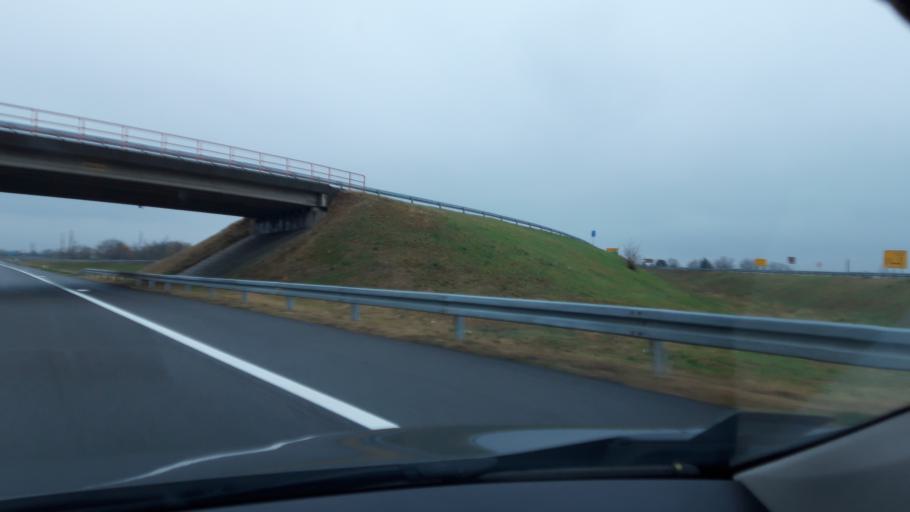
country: HU
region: Csongrad
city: Asotthalom
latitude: 46.1069
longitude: 19.7946
